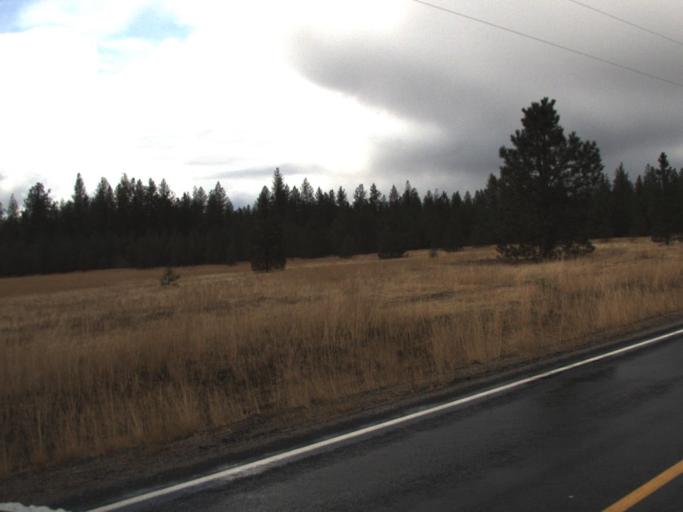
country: US
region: Washington
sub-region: Spokane County
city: Deer Park
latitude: 48.0023
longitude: -117.7265
